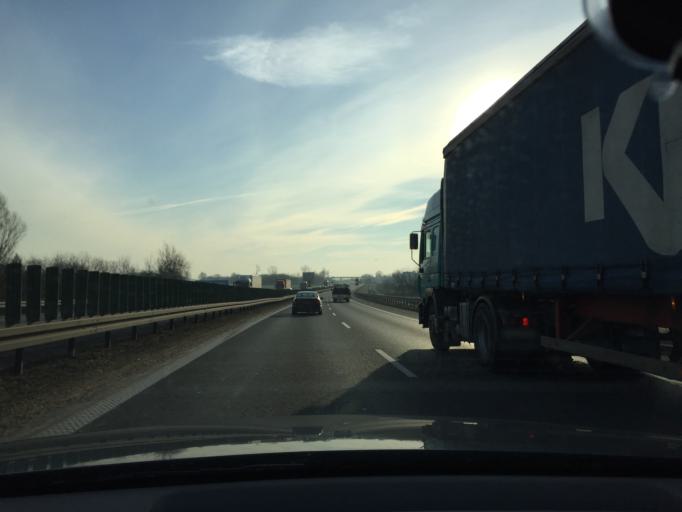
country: PL
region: Lesser Poland Voivodeship
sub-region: Powiat krakowski
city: Balice
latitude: 50.0692
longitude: 19.8105
